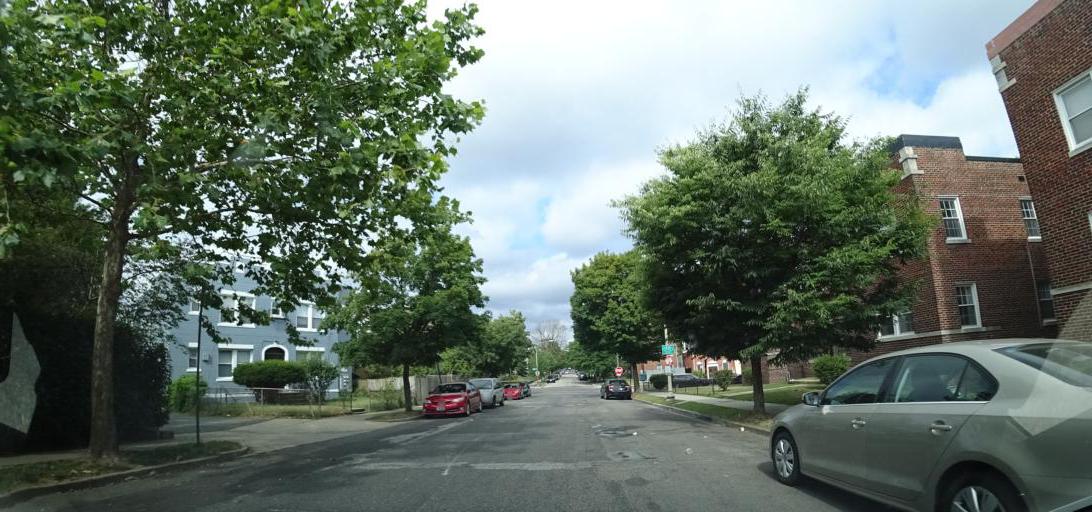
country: US
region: Maryland
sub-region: Montgomery County
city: Takoma Park
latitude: 38.9386
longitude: -77.0275
